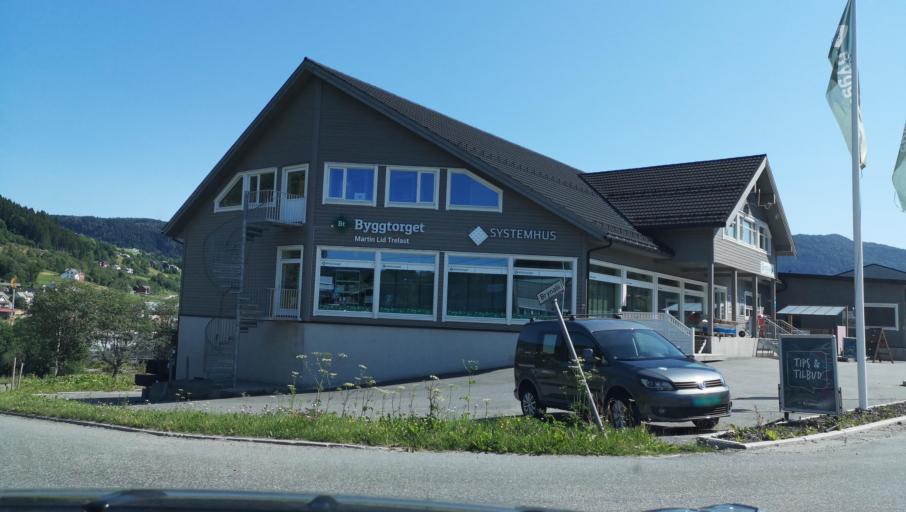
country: NO
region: Hordaland
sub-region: Voss
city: Voss
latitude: 60.6344
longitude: 6.4641
